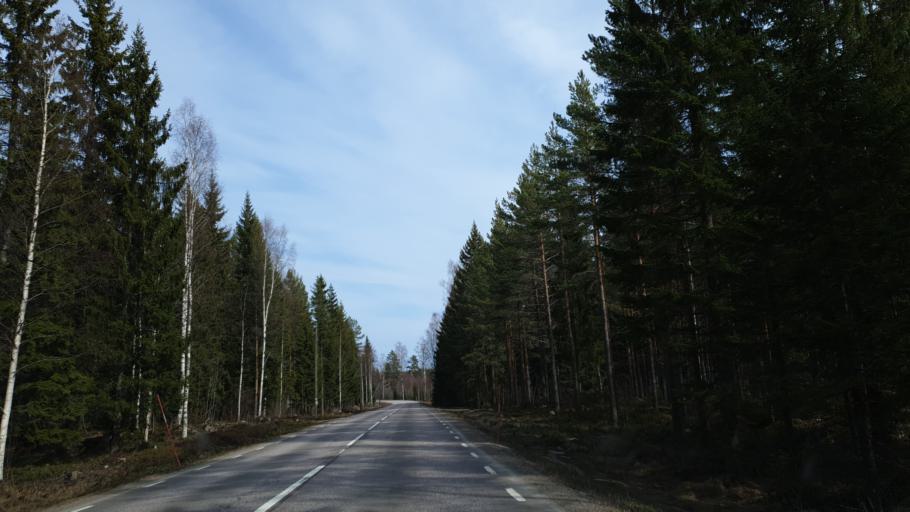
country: SE
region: Gaevleborg
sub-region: Gavle Kommun
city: Norrsundet
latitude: 60.9831
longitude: 17.0715
